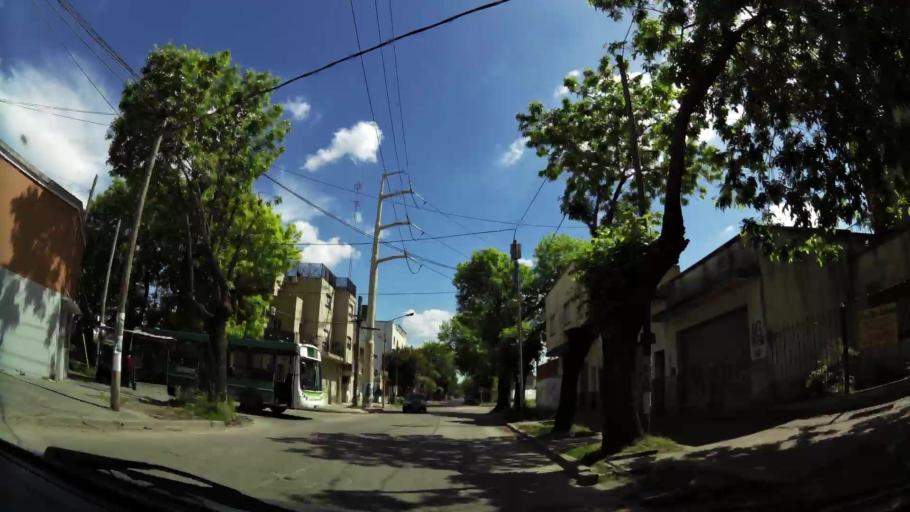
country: AR
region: Buenos Aires
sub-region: Partido de Quilmes
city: Quilmes
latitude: -34.8164
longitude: -58.2726
